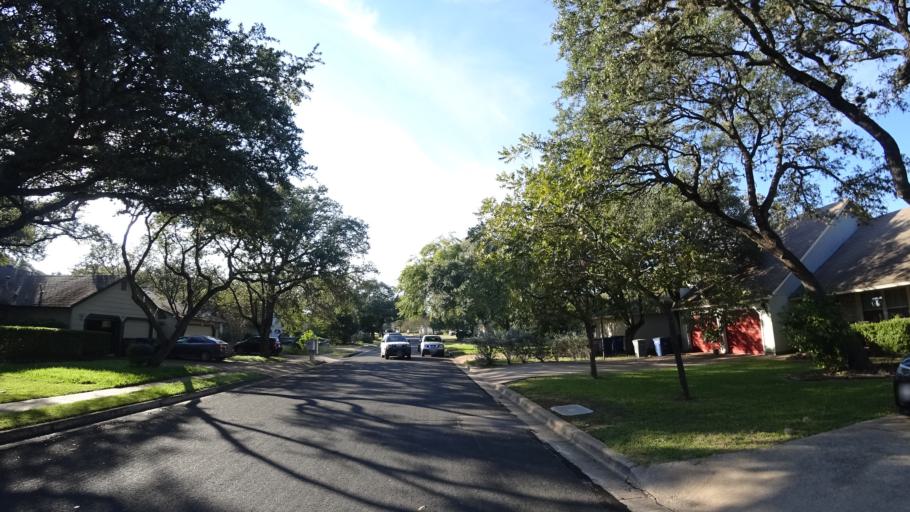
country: US
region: Texas
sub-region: Travis County
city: Shady Hollow
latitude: 30.2107
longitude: -97.8472
